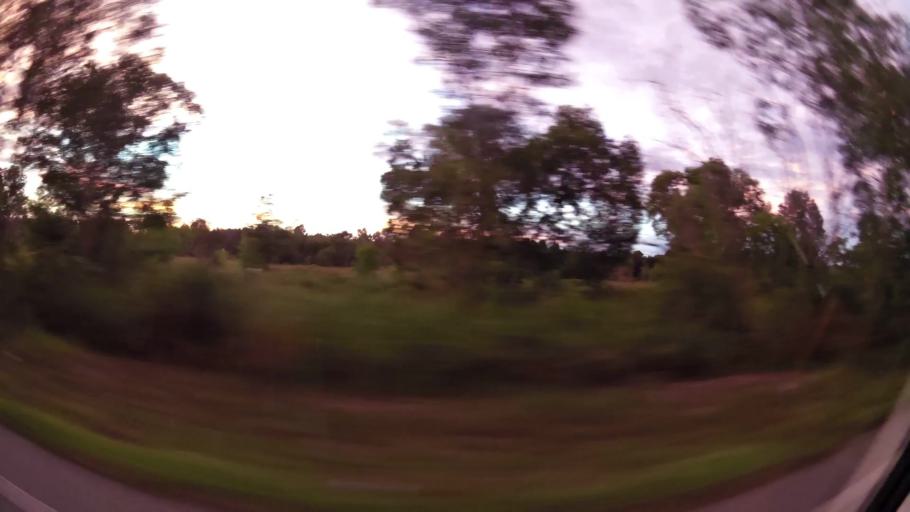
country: BN
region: Belait
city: Seria
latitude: 4.6381
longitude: 114.3946
